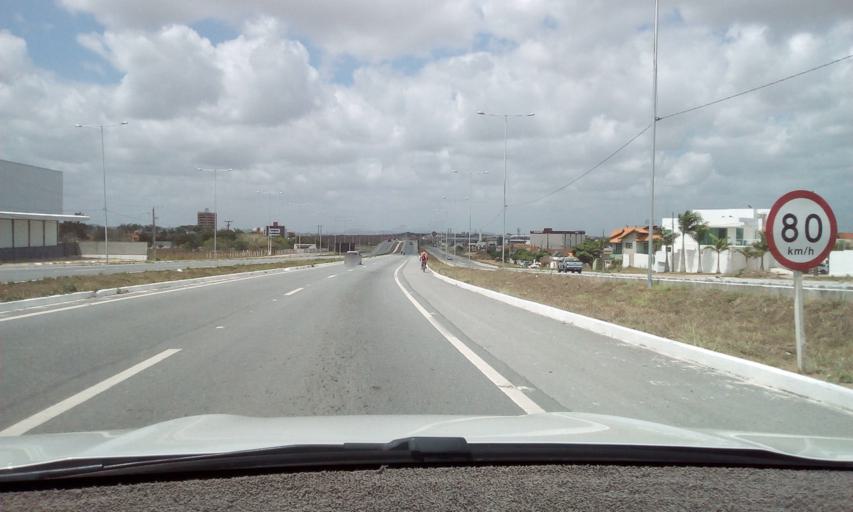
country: BR
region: Paraiba
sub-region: Campina Grande
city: Campina Grande
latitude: -7.2513
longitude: -35.8725
